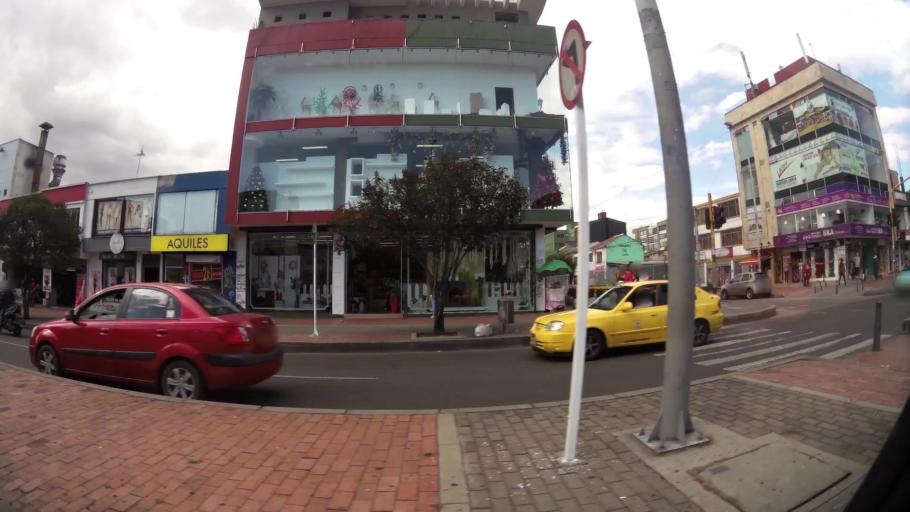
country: CO
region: Bogota D.C.
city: Bogota
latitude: 4.6413
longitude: -74.0715
